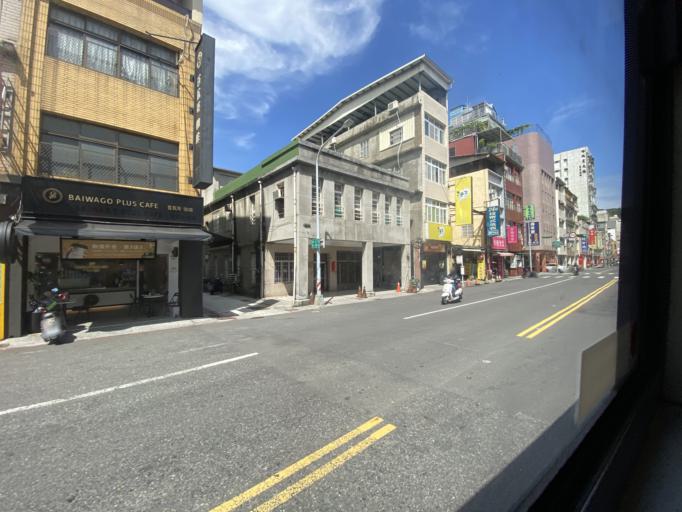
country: TW
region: Kaohsiung
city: Kaohsiung
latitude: 22.6224
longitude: 120.2731
